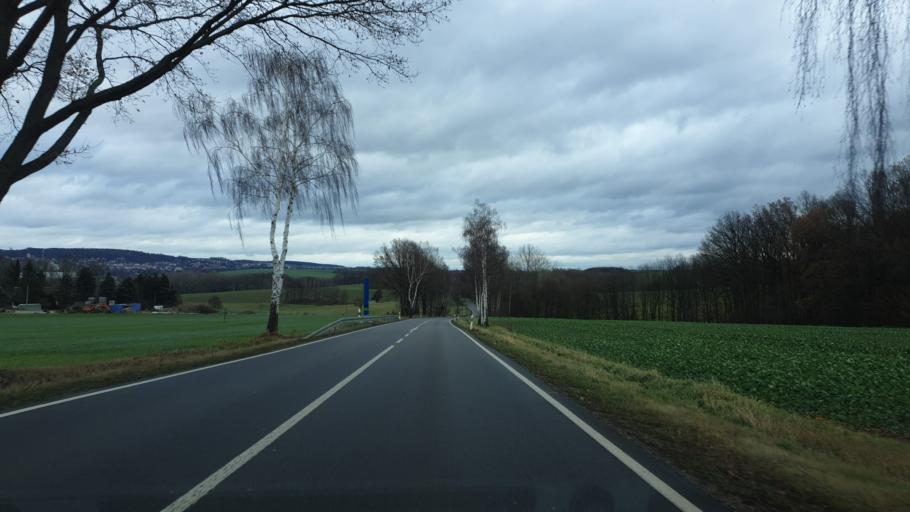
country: DE
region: Saxony
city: Bernsdorf
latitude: 50.7724
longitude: 12.6723
